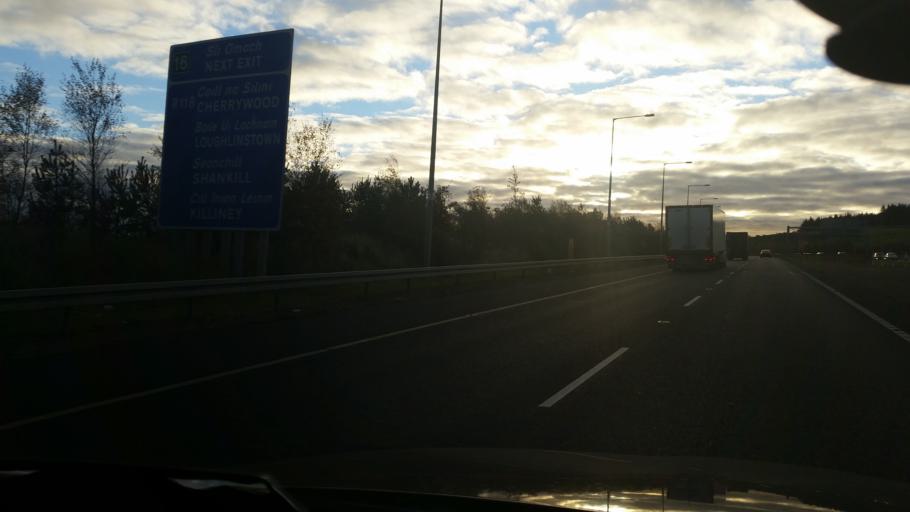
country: IE
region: Leinster
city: Foxrock
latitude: 53.2476
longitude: -6.1646
